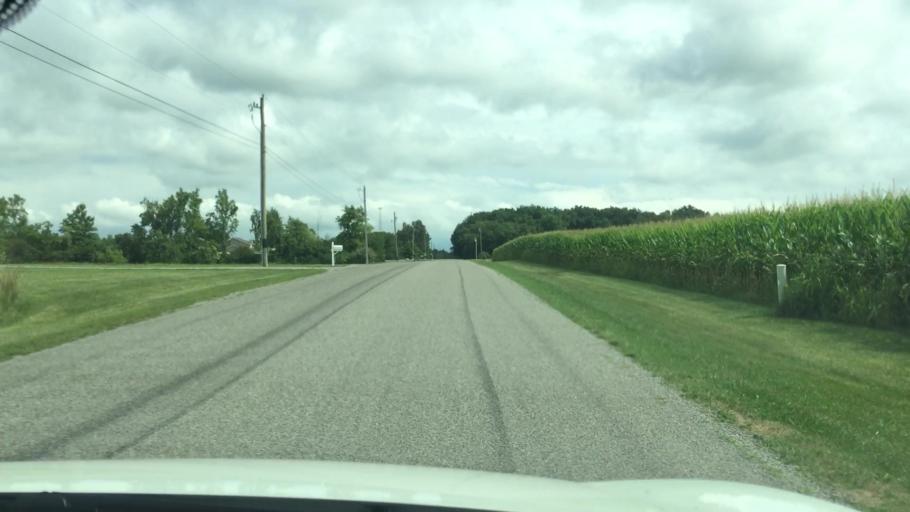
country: US
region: Ohio
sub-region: Champaign County
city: North Lewisburg
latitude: 40.2696
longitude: -83.5400
